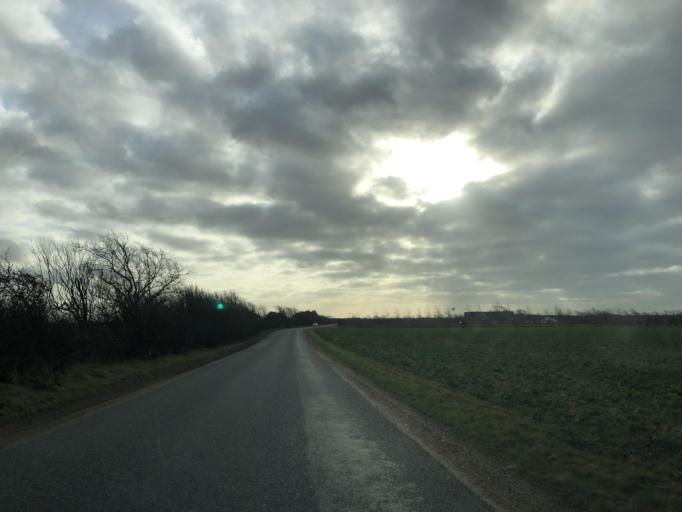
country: DK
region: Central Jutland
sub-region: Lemvig Kommune
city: Lemvig
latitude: 56.4353
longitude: 8.3308
